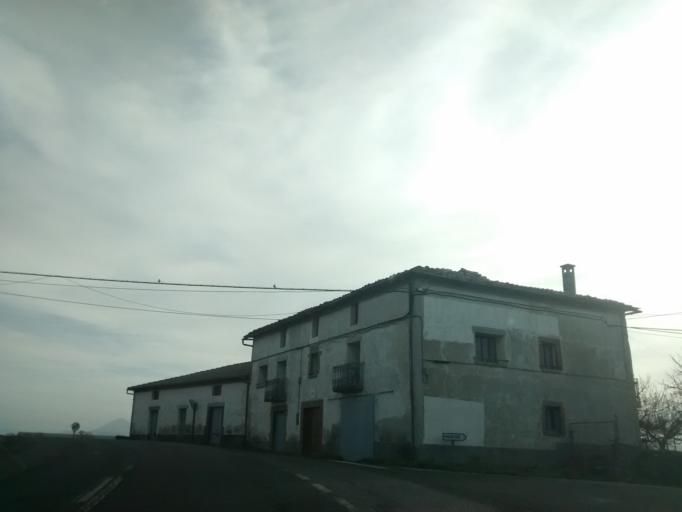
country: ES
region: Aragon
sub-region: Provincia de Zaragoza
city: Mianos
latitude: 42.5996
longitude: -0.8595
